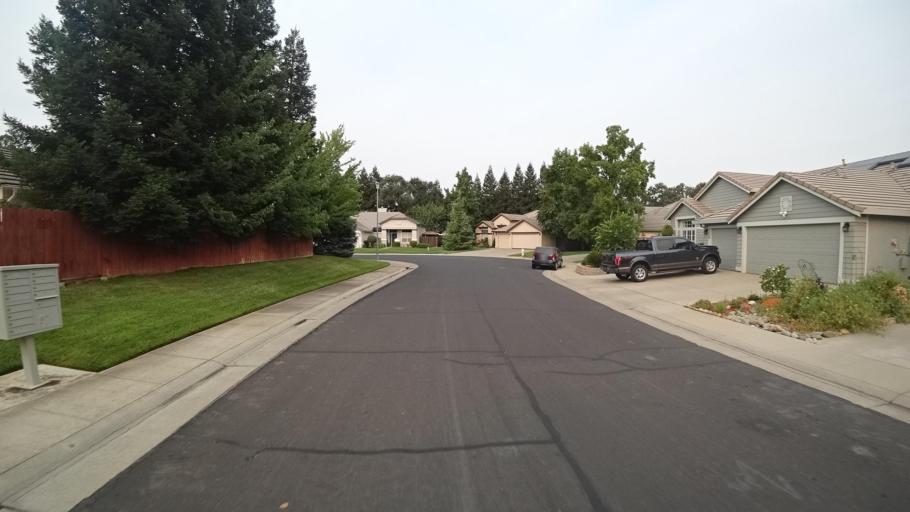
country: US
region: California
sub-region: Sacramento County
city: Elk Grove
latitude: 38.4122
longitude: -121.3960
